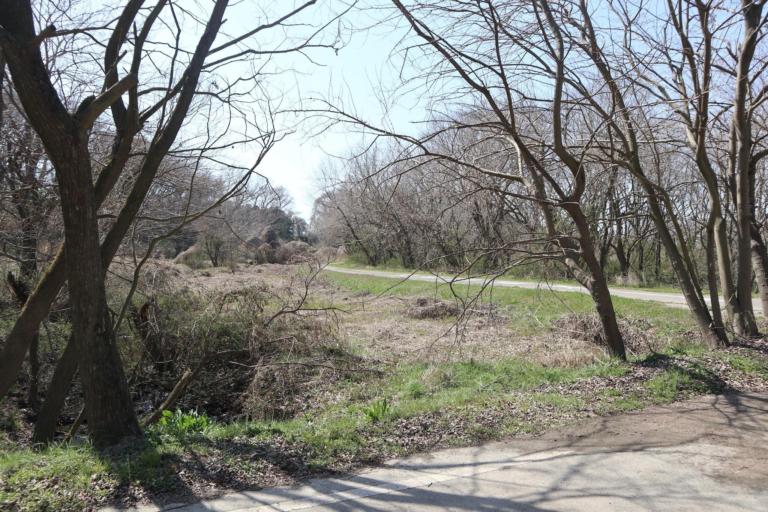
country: JP
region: Ibaraki
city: Koga
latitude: 36.2191
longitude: 139.7082
